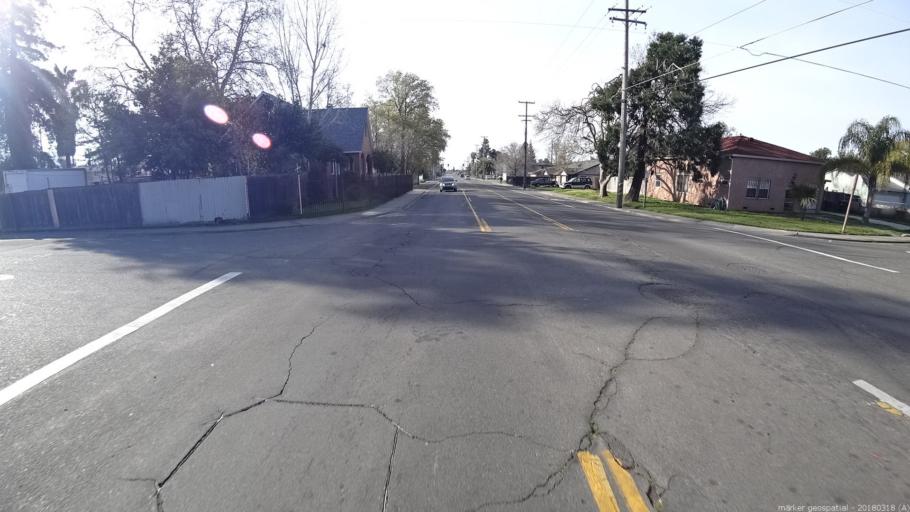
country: US
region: California
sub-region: Sacramento County
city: Parkway
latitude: 38.5149
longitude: -121.4646
